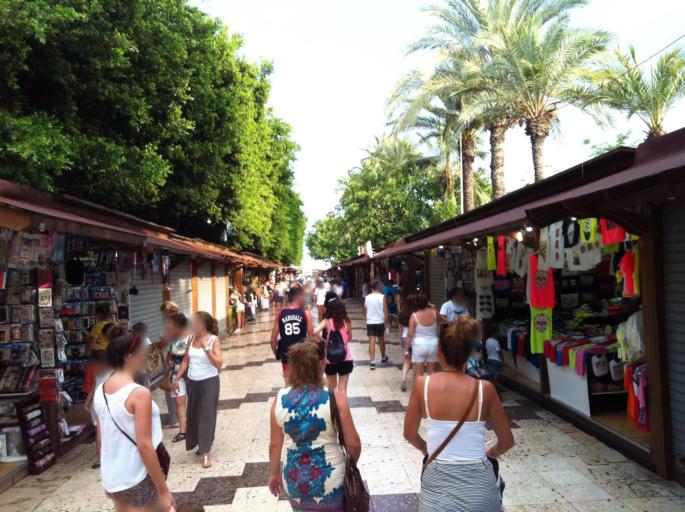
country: ES
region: Valencia
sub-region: Provincia de Alicante
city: Torrevieja
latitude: 37.9751
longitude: -0.6794
